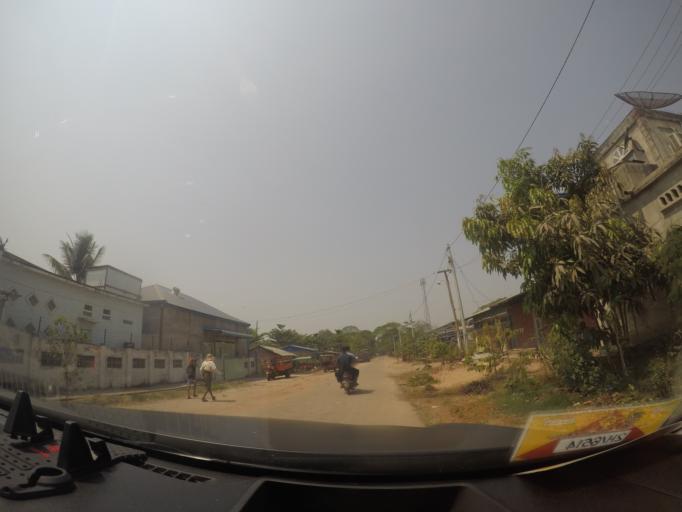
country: MM
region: Magway
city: Myaydo
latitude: 19.3426
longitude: 95.2175
